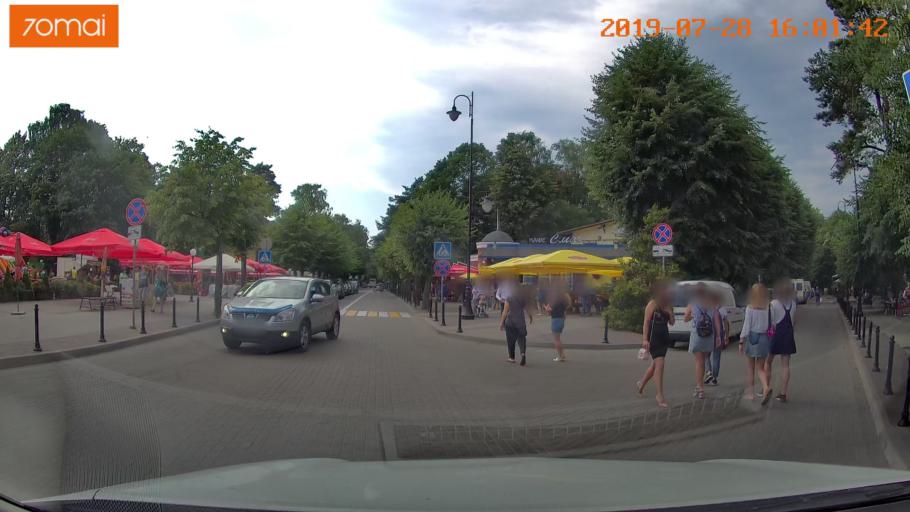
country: RU
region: Kaliningrad
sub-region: Gorod Svetlogorsk
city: Svetlogorsk
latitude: 54.9441
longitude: 20.1532
